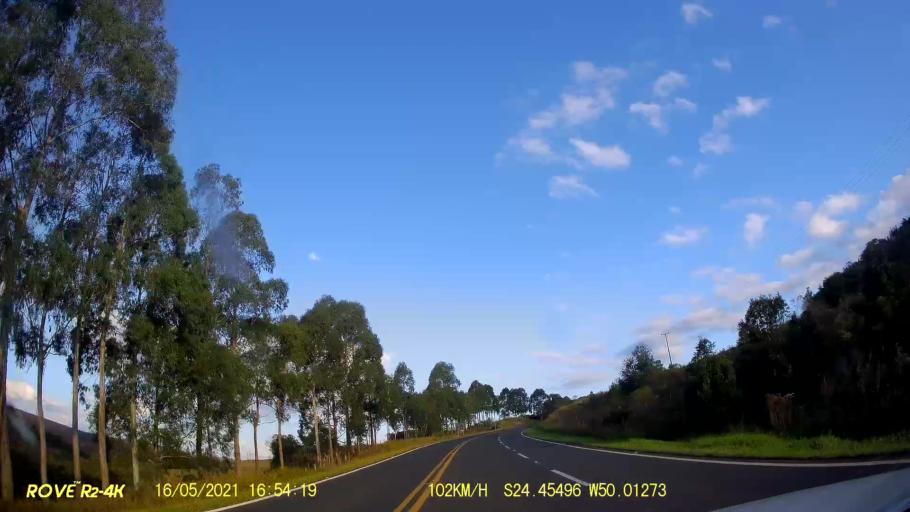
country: BR
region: Parana
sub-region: Pirai Do Sul
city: Pirai do Sul
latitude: -24.4550
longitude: -50.0129
